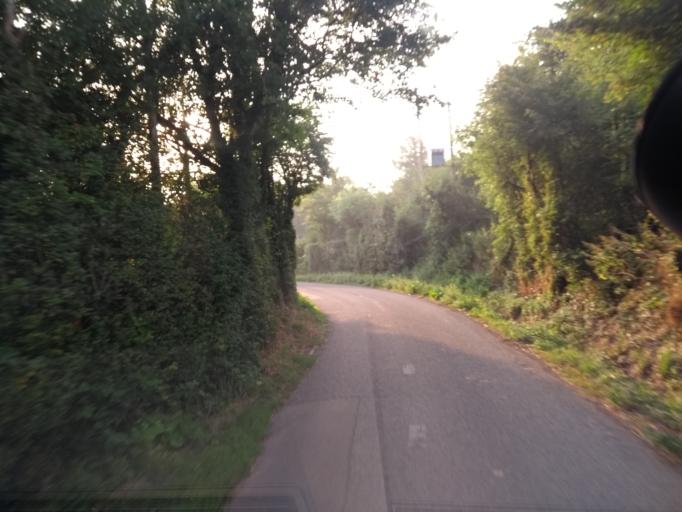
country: GB
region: England
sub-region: Somerset
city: Curry Rivel
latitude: 50.9944
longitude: -2.9238
